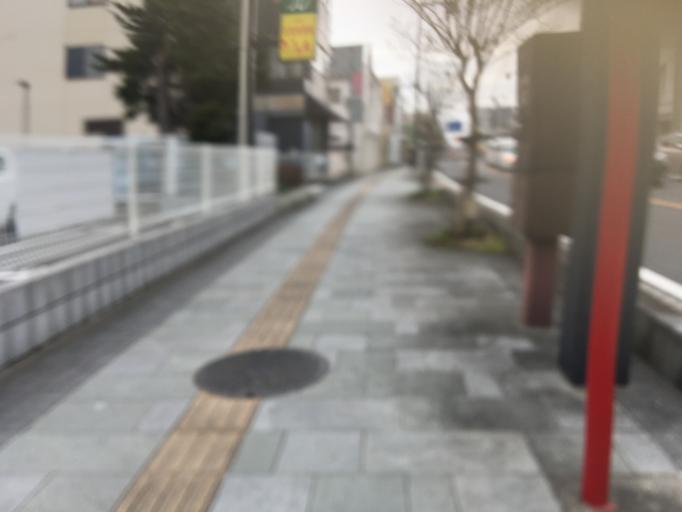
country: JP
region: Saitama
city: Kazo
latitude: 36.1257
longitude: 139.5996
